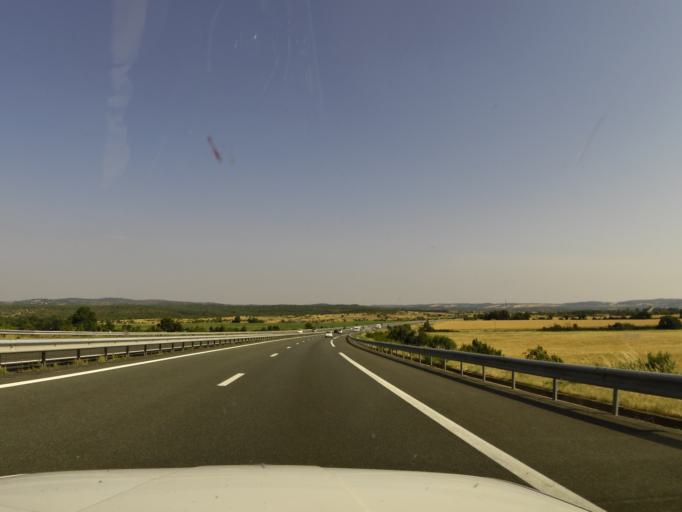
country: FR
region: Midi-Pyrenees
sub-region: Departement de l'Aveyron
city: La Cavalerie
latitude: 43.9714
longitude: 3.2071
